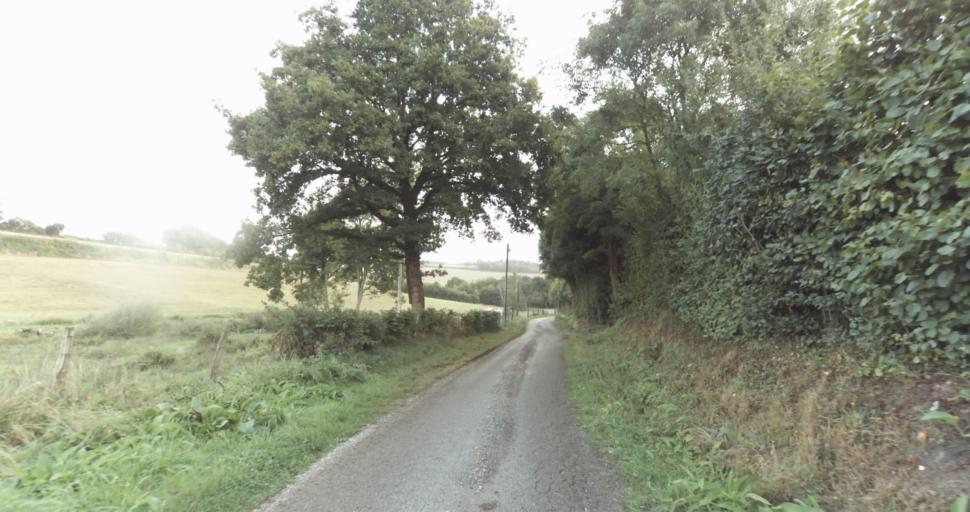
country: FR
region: Lower Normandy
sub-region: Departement de l'Orne
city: Vimoutiers
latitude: 48.8839
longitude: 0.2716
